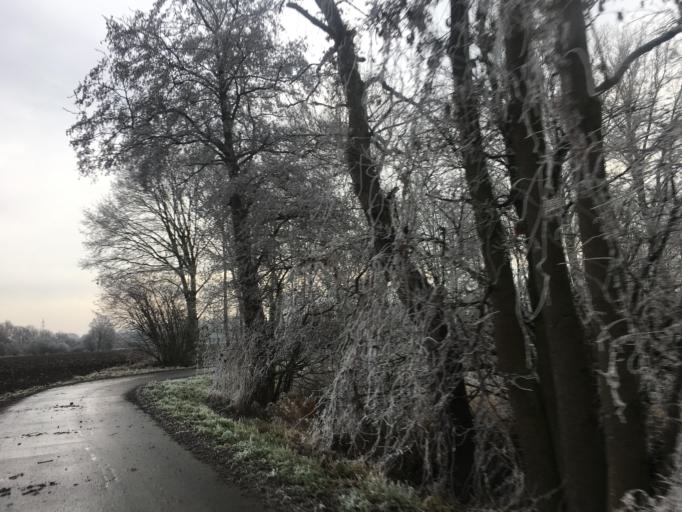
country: DE
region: North Rhine-Westphalia
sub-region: Regierungsbezirk Munster
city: Greven
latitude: 52.0600
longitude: 7.5542
